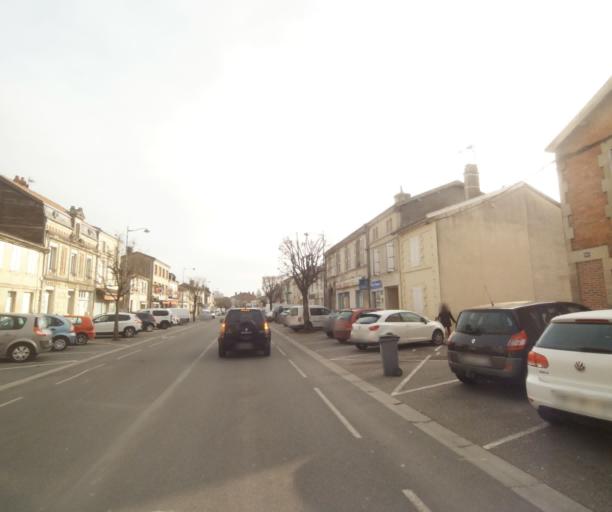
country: FR
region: Champagne-Ardenne
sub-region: Departement de la Haute-Marne
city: Saint-Dizier
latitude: 48.6377
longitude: 4.9388
